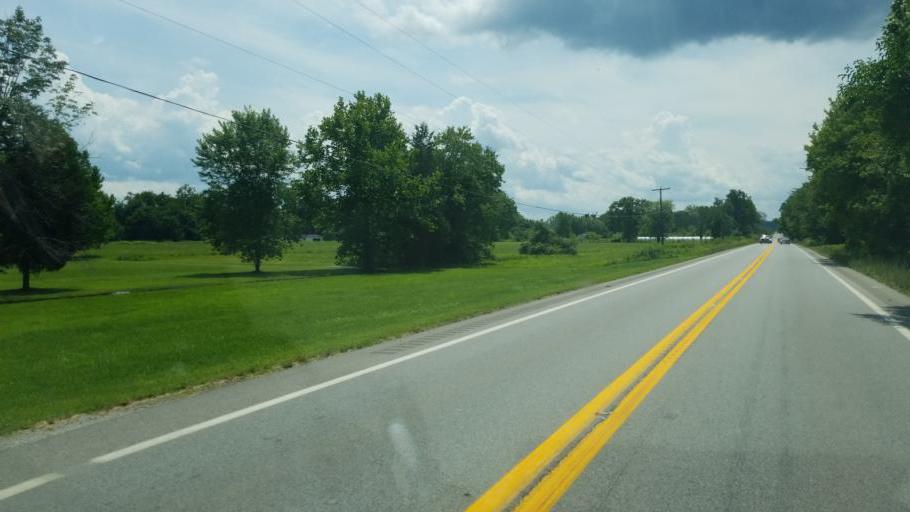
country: US
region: West Virginia
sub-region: Putnam County
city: Buffalo
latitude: 38.6206
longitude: -81.9875
